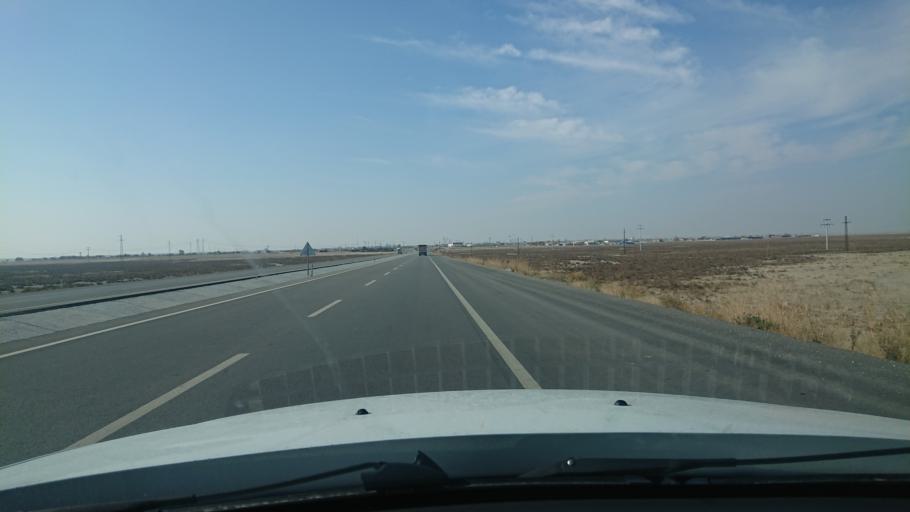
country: TR
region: Aksaray
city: Sultanhani
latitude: 38.2536
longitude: 33.4925
